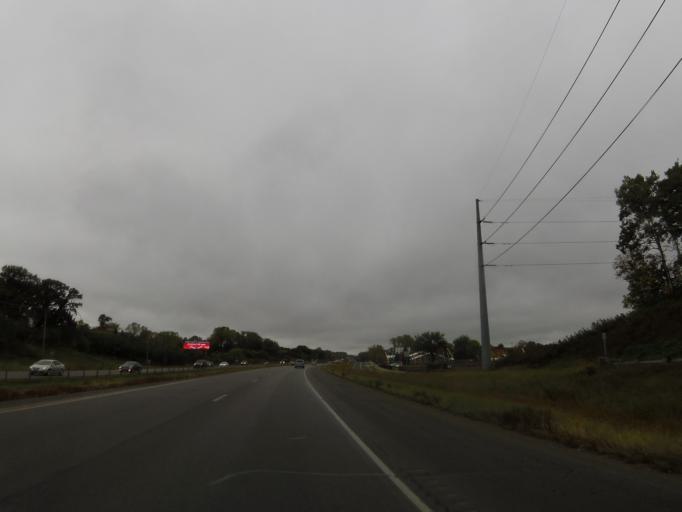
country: US
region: Minnesota
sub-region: Dakota County
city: Inver Grove Heights
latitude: 44.7931
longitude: -93.0366
